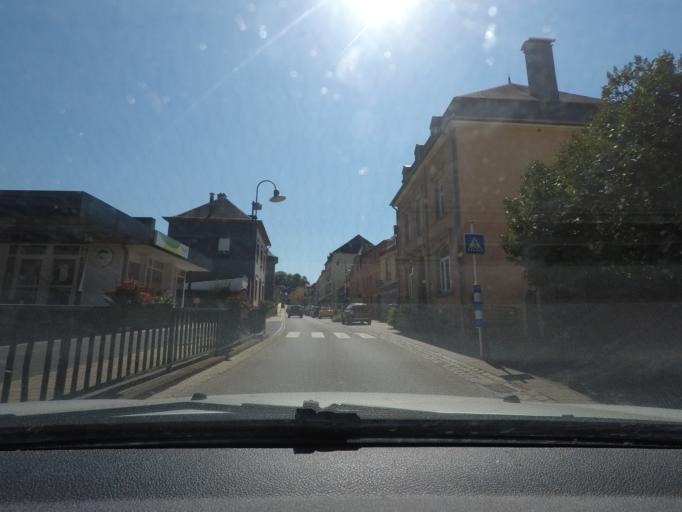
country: LU
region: Diekirch
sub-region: Canton de Redange
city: Redange-sur-Attert
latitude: 49.7643
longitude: 5.8841
